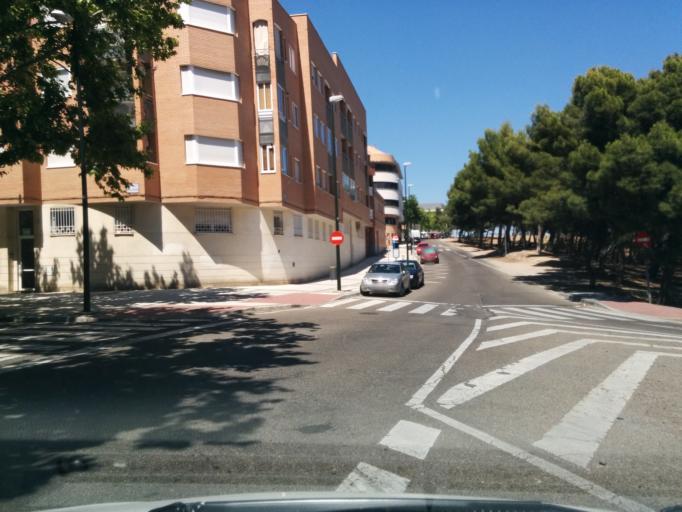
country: ES
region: Aragon
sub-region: Provincia de Zaragoza
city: Zaragoza
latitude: 41.6249
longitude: -0.8750
